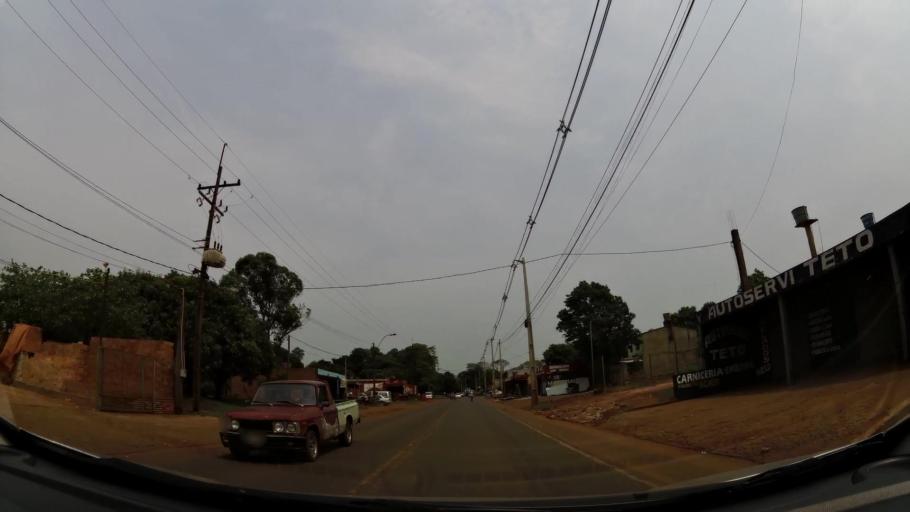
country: PY
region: Alto Parana
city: Presidente Franco
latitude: -25.5529
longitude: -54.6372
